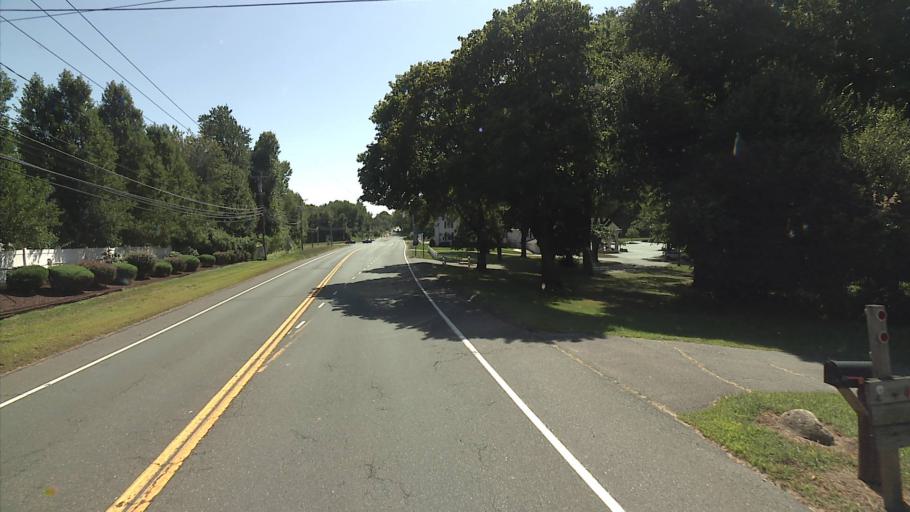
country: US
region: Connecticut
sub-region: Hartford County
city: Thompsonville
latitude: 41.9896
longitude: -72.6134
